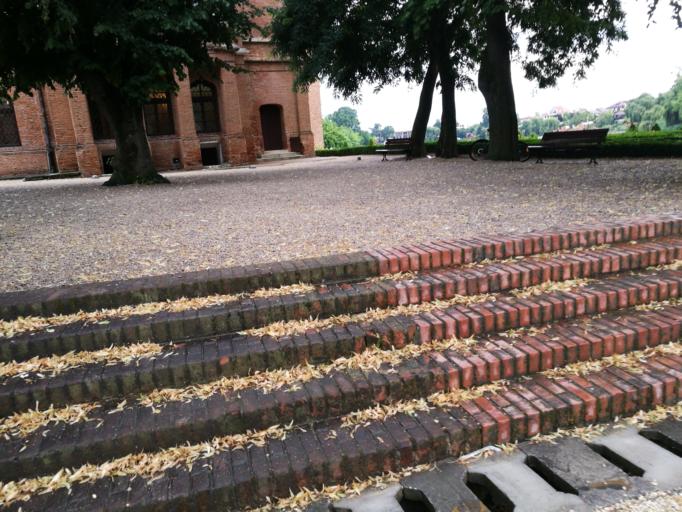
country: RO
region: Ilfov
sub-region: Comuna Mogosoaia
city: Mogosoaia
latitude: 44.5281
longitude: 25.9926
